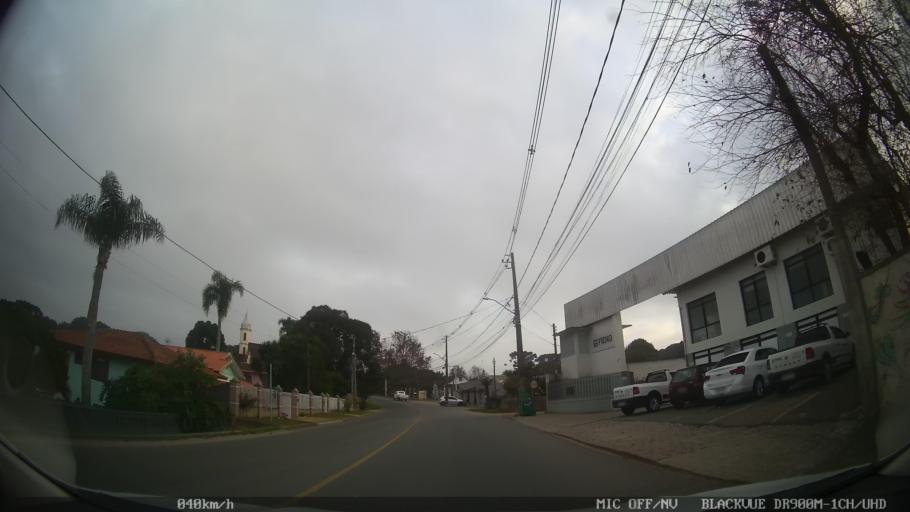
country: BR
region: Parana
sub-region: Almirante Tamandare
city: Almirante Tamandare
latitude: -25.3786
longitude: -49.3158
